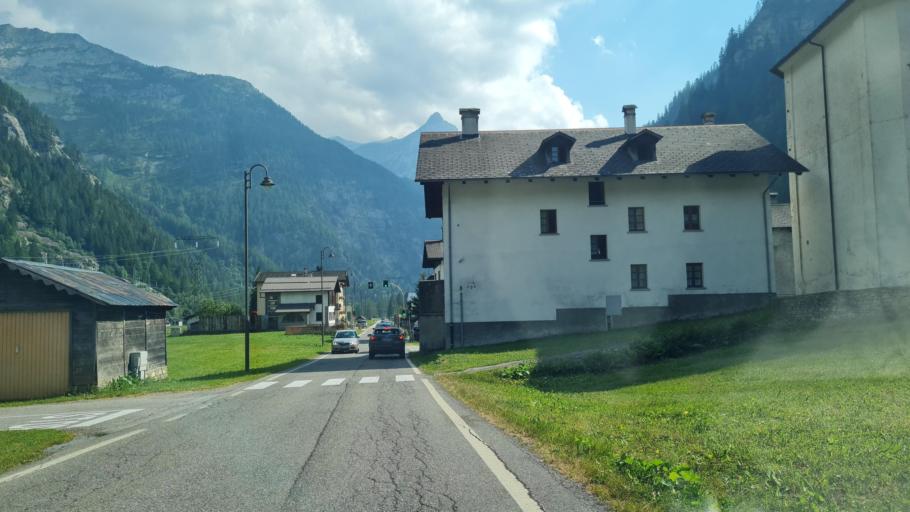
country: IT
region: Piedmont
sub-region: Provincia Verbano-Cusio-Ossola
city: Formazza
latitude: 46.3540
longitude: 8.4280
